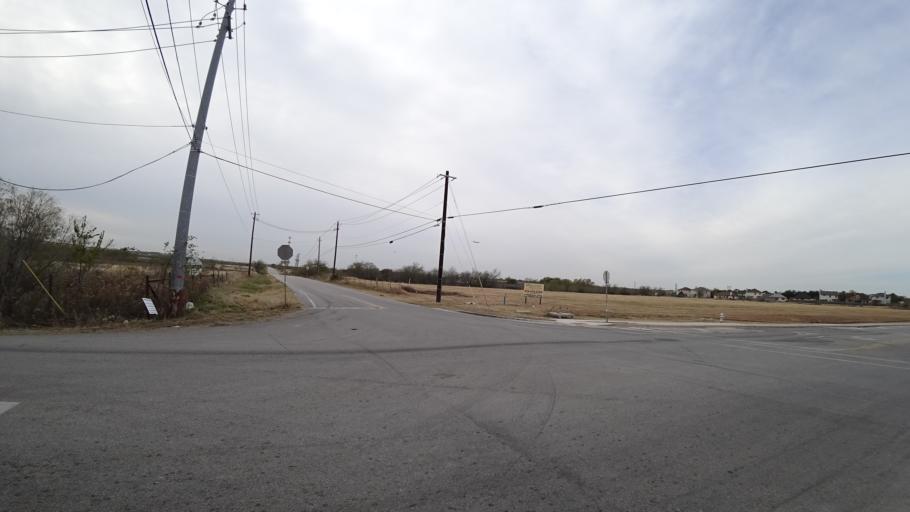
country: US
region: Texas
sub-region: Travis County
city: Garfield
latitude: 30.1540
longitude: -97.6396
